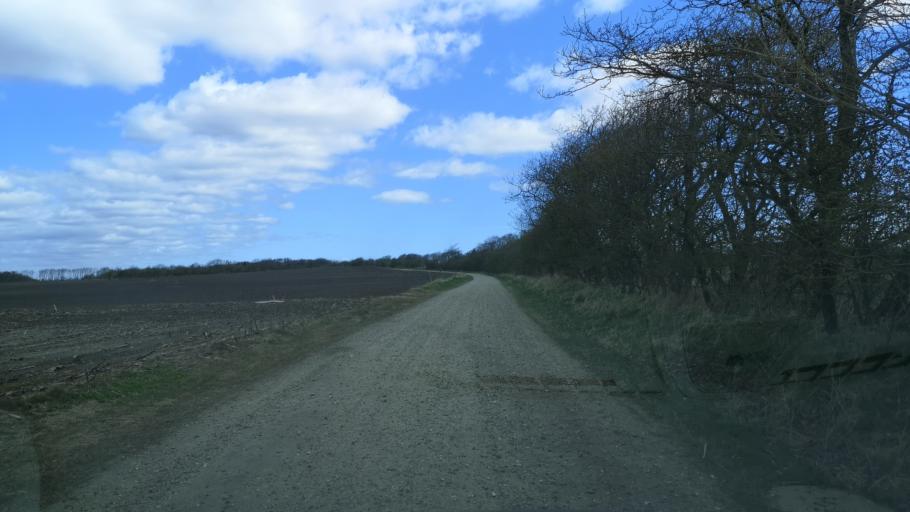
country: DK
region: Central Jutland
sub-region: Ringkobing-Skjern Kommune
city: Skjern
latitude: 55.9814
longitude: 8.5114
